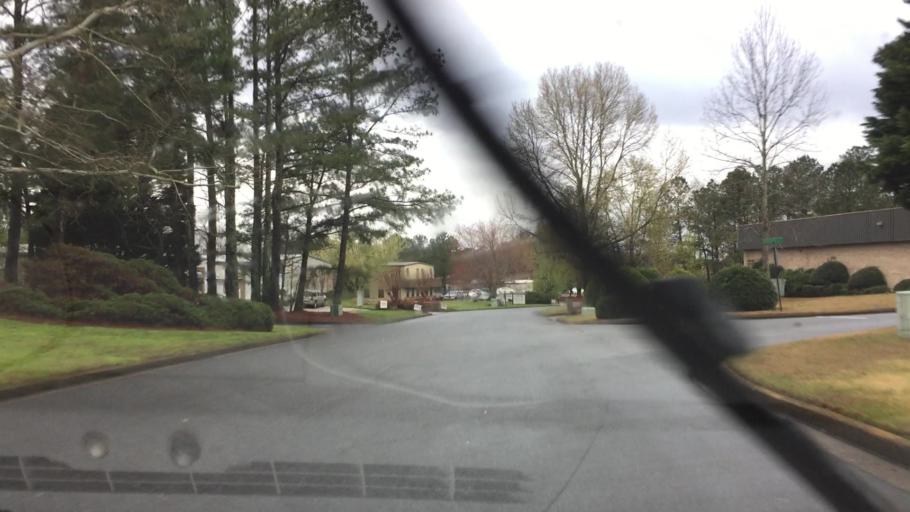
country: US
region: Georgia
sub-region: Fulton County
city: Milton
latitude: 34.1361
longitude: -84.2522
